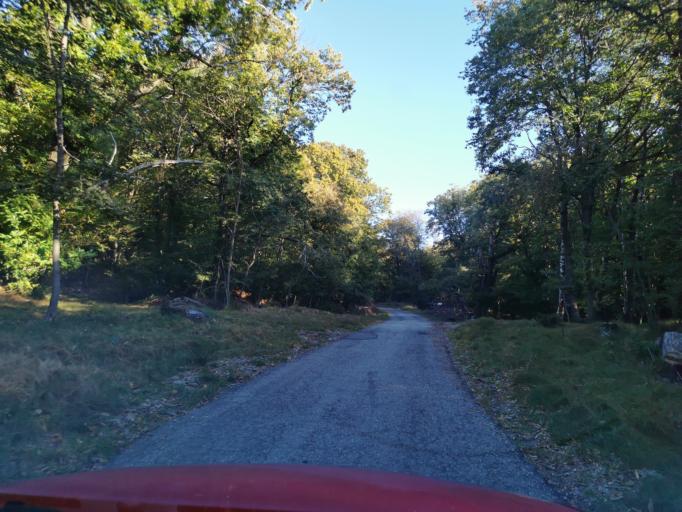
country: IT
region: Lombardy
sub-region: Provincia di Como
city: San Siro
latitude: 46.0756
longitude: 9.2563
